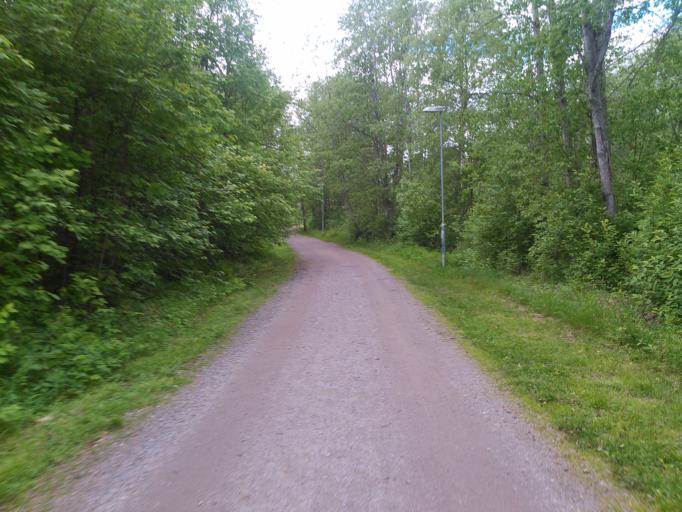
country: SE
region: Vaesterbotten
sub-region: Umea Kommun
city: Umea
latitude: 63.8247
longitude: 20.2379
